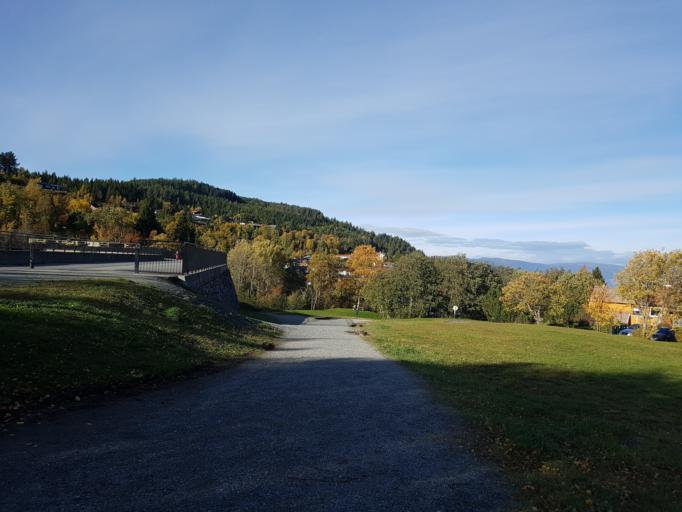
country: NO
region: Sor-Trondelag
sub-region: Trondheim
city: Trondheim
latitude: 63.4227
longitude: 10.3495
